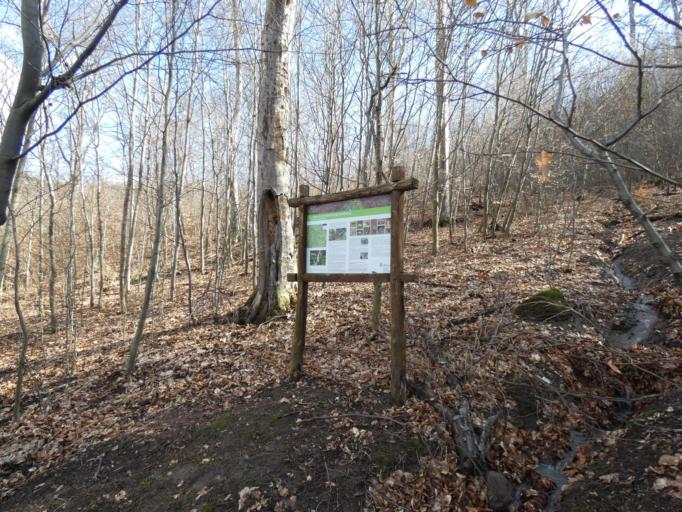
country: HU
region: Pest
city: Visegrad
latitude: 47.7630
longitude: 19.0057
